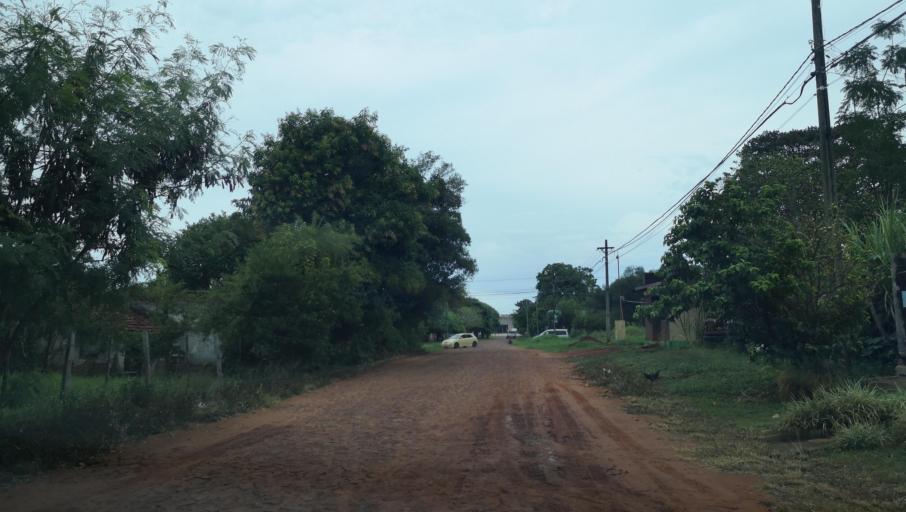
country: PY
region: Misiones
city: Santa Maria
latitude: -26.8825
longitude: -57.0291
